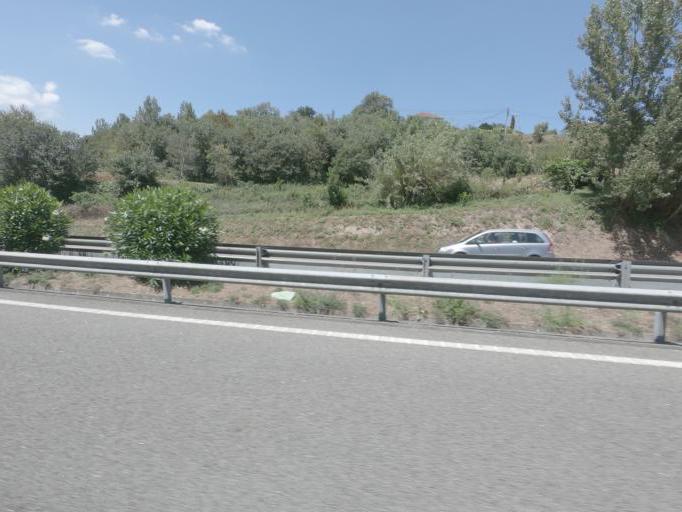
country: PT
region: Porto
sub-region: Marco de Canaveses
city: Marco de Canavezes
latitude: 41.2188
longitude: -8.1524
